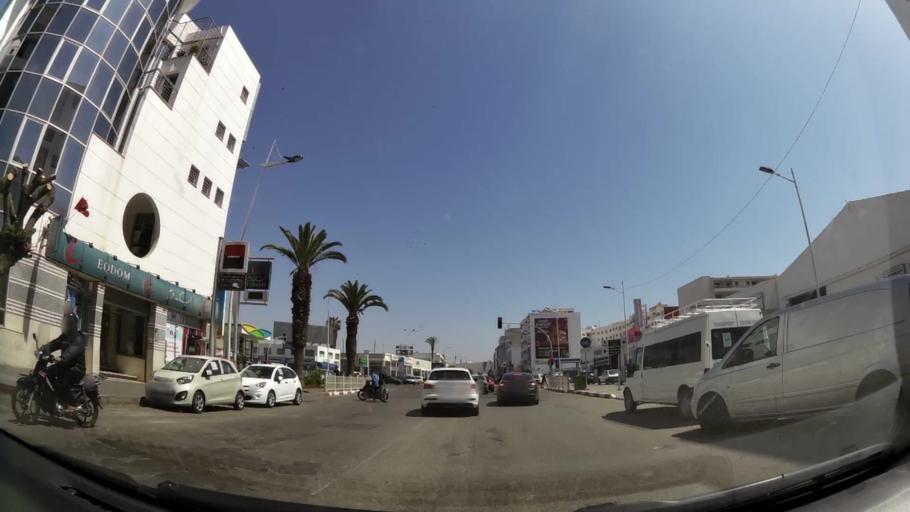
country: MA
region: Souss-Massa-Draa
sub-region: Agadir-Ida-ou-Tnan
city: Agadir
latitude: 30.4124
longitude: -9.5916
